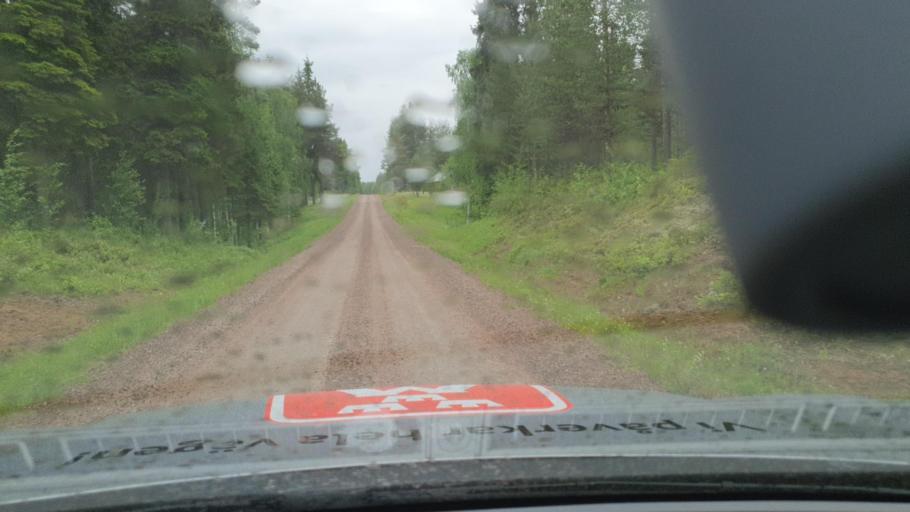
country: SE
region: Norrbotten
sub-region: Overkalix Kommun
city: OEverkalix
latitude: 66.5433
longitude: 22.7438
